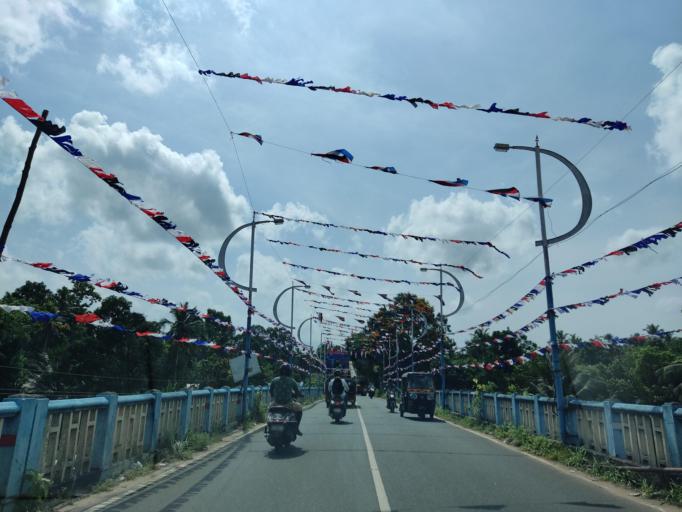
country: IN
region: Kerala
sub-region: Alappuzha
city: Mavelikara
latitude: 9.2629
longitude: 76.5424
